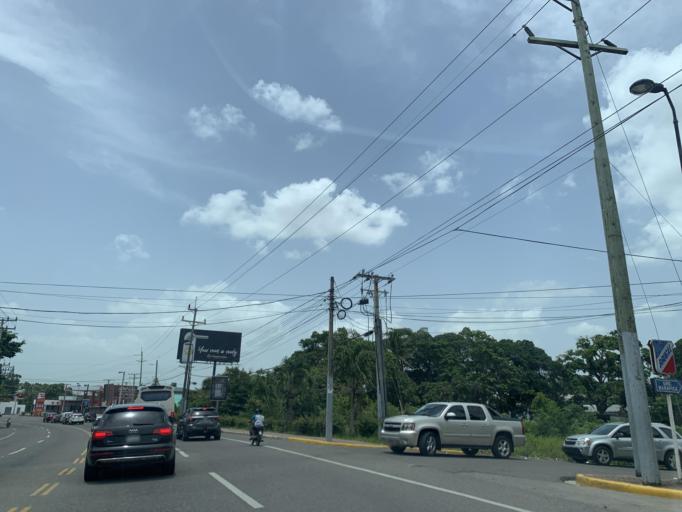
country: DO
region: Puerto Plata
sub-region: Puerto Plata
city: Puerto Plata
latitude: 19.7776
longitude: -70.6673
